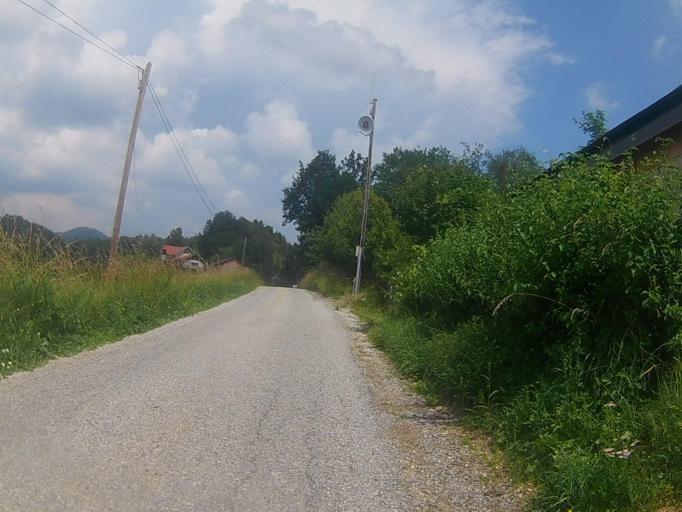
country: SI
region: Maribor
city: Bresternica
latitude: 46.5865
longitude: 15.5921
